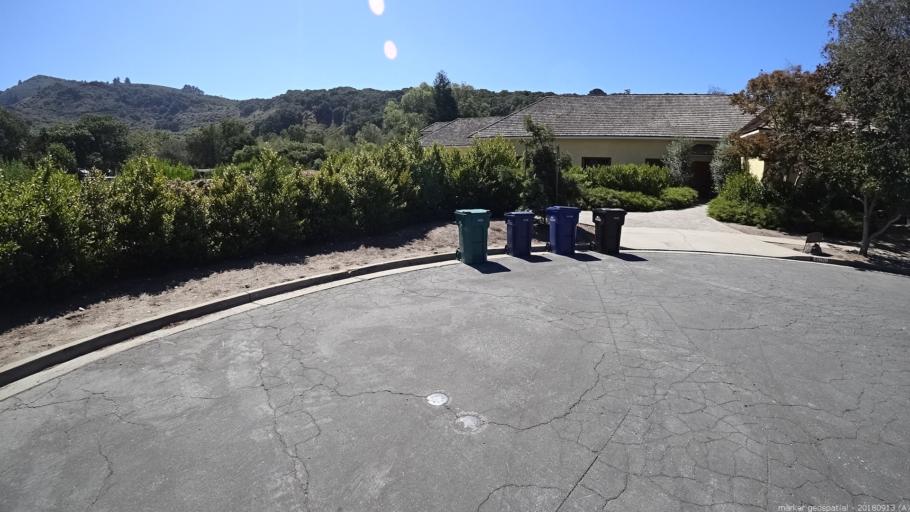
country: US
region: California
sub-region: Monterey County
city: Del Rey Oaks
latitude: 36.5286
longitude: -121.8552
